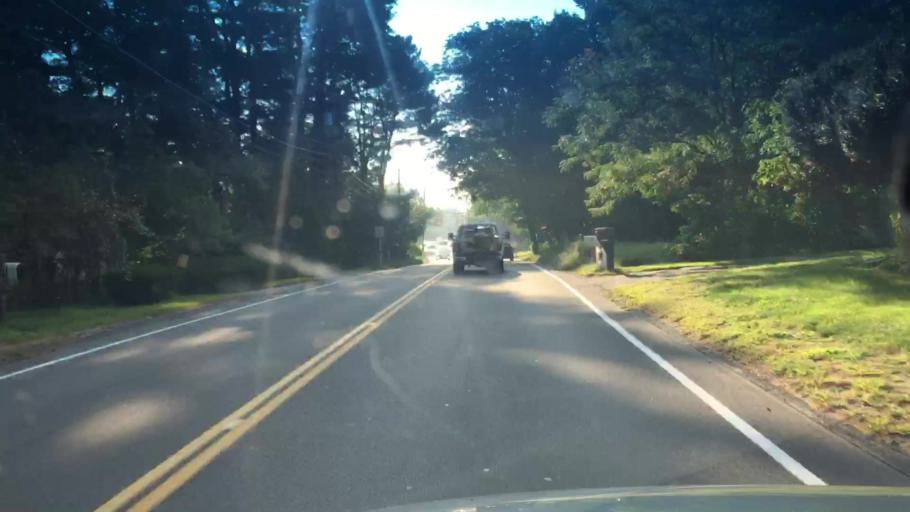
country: US
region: Massachusetts
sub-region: Norfolk County
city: Walpole
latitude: 42.1530
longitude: -71.2667
